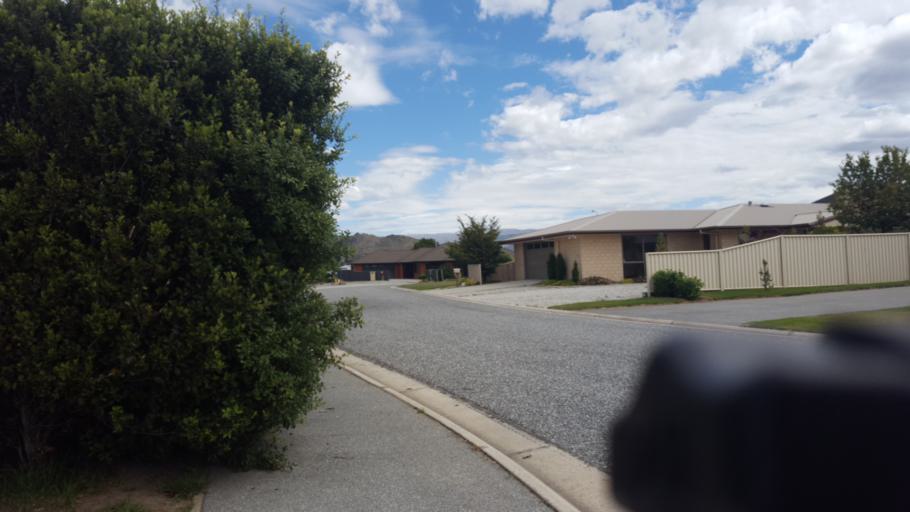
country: NZ
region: Otago
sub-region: Queenstown-Lakes District
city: Wanaka
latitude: -45.0385
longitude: 169.2169
